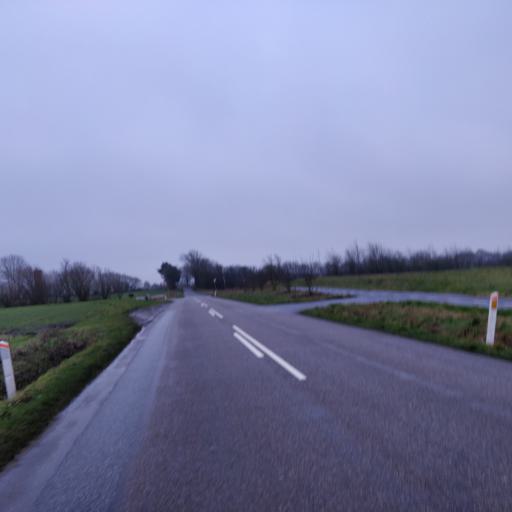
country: DK
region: South Denmark
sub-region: Sonderborg Kommune
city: Augustenborg
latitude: 54.9714
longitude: 9.9393
